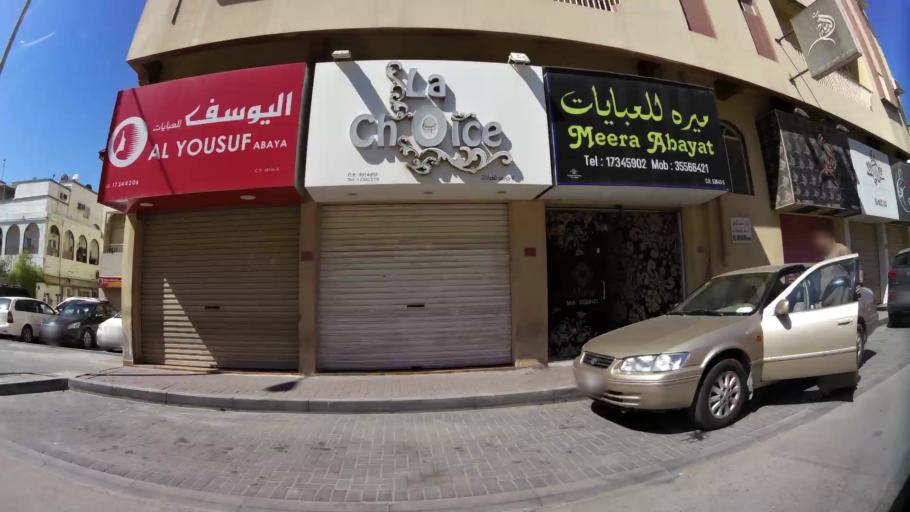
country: BH
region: Muharraq
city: Al Muharraq
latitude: 26.2561
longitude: 50.6192
